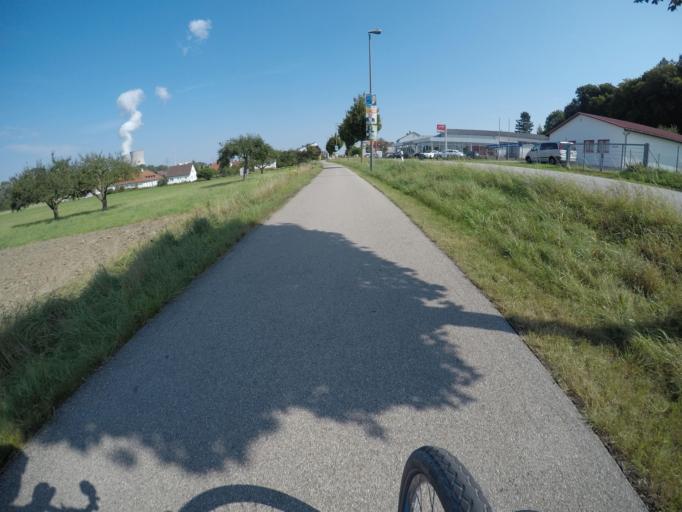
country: DE
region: Bavaria
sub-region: Swabia
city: Gundremmingen
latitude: 48.4969
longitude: 10.3966
